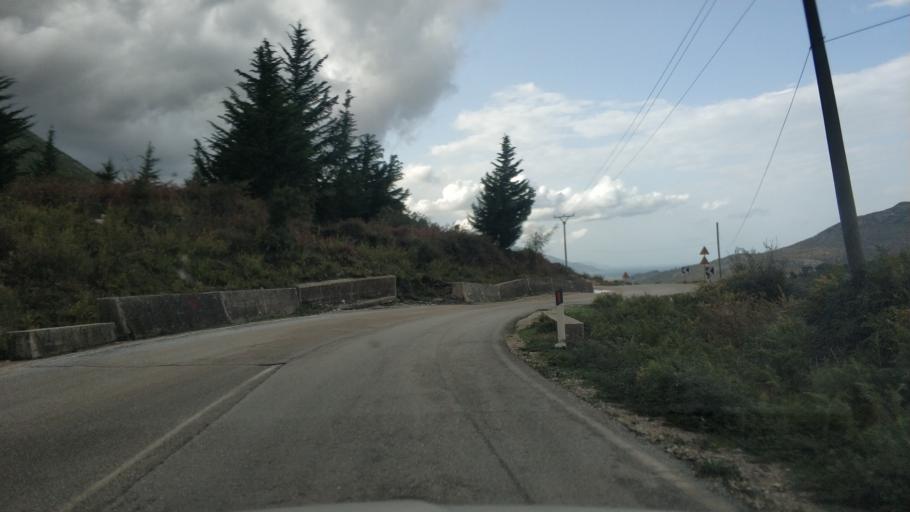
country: AL
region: Vlore
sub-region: Rrethi i Vlores
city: Orikum
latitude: 40.2615
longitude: 19.5234
